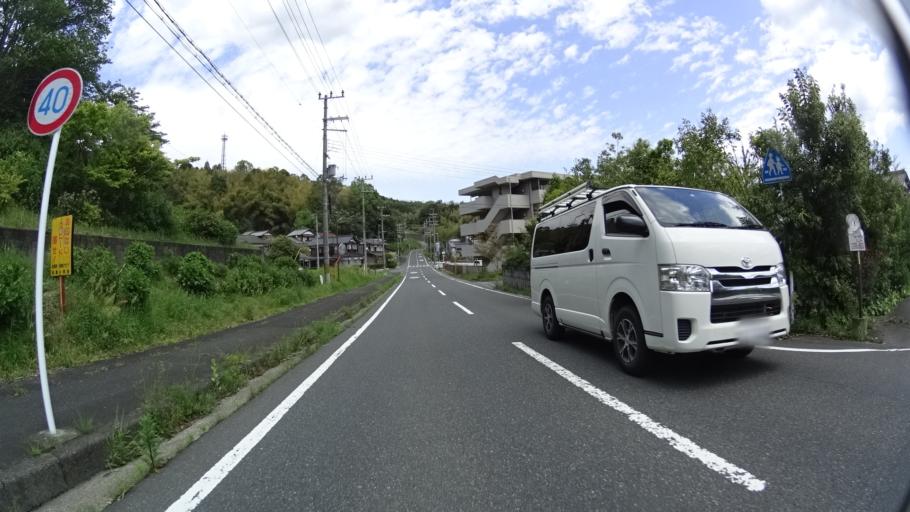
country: JP
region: Kyoto
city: Miyazu
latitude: 35.5673
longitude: 135.1474
